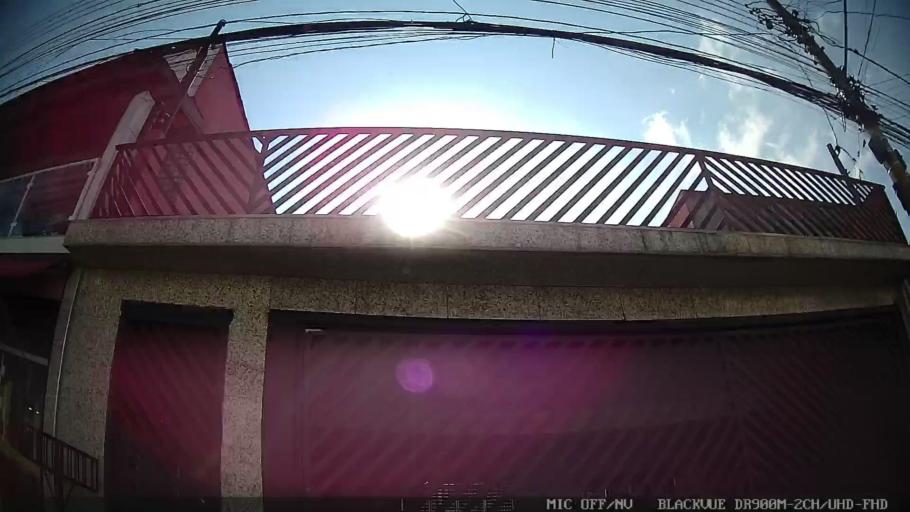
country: BR
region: Sao Paulo
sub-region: Ferraz De Vasconcelos
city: Ferraz de Vasconcelos
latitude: -23.5207
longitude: -46.4301
